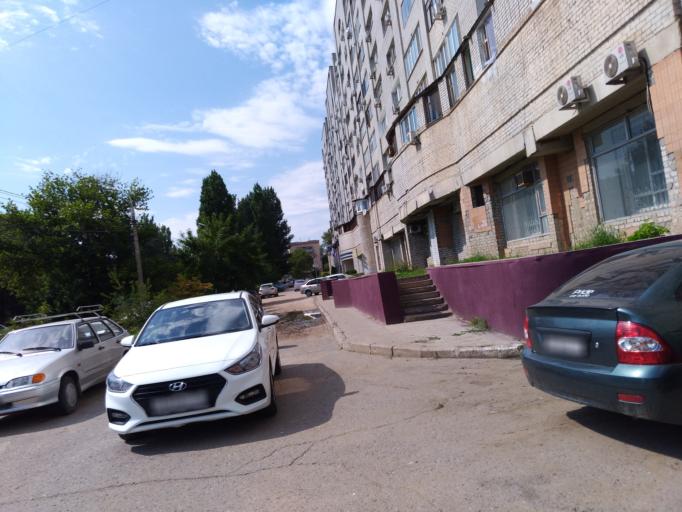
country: RU
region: Volgograd
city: Volgograd
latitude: 48.7122
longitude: 44.5016
